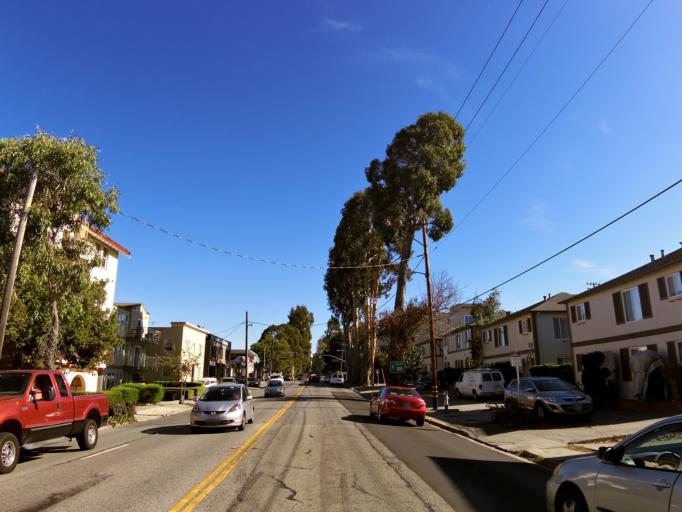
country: US
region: California
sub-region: San Mateo County
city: Burlingame
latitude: 37.5848
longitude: -122.3675
